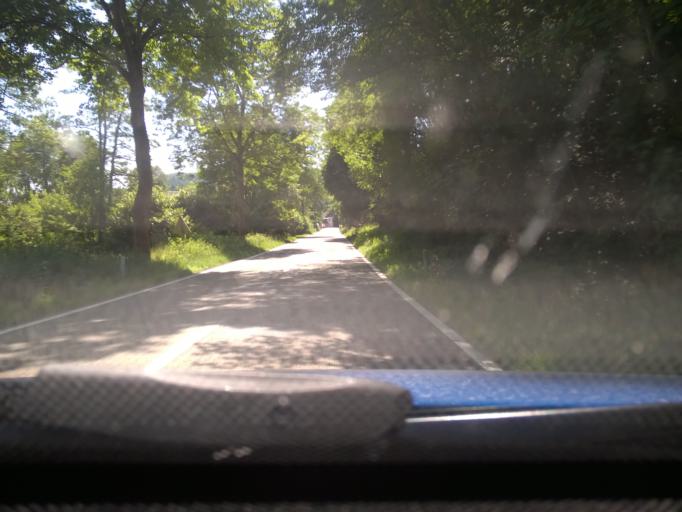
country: BE
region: Wallonia
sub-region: Province du Luxembourg
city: Wellin
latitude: 50.0671
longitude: 5.1370
